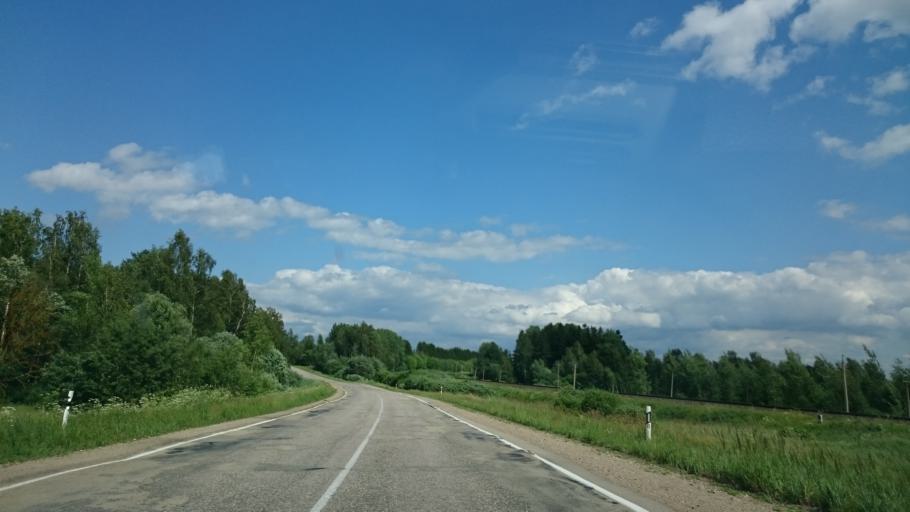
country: LV
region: Ludzas Rajons
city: Ludza
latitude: 56.5343
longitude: 27.6074
